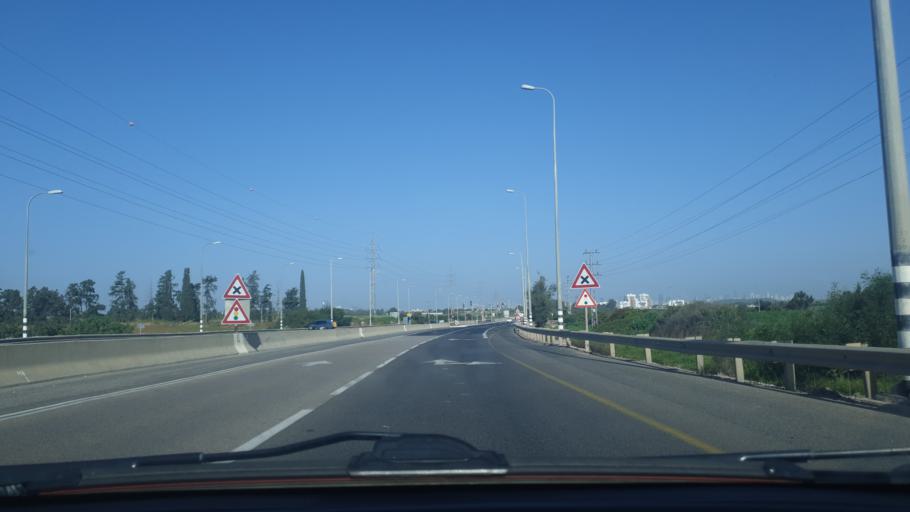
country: IL
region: Central District
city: Kefar Habad
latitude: 31.9771
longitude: 34.8382
